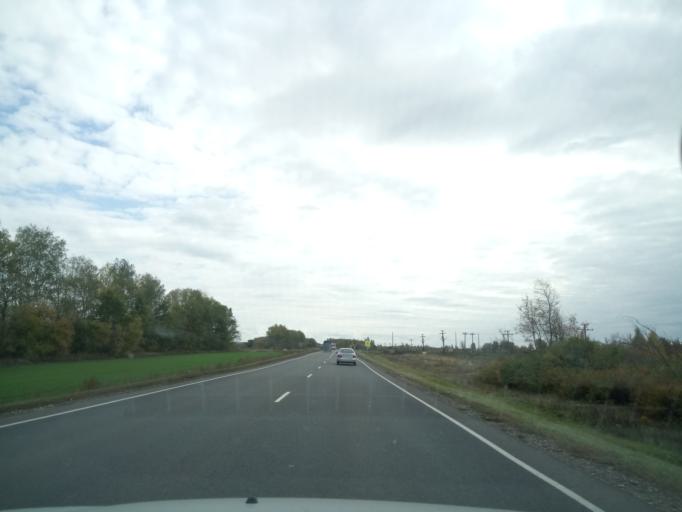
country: RU
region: Nizjnij Novgorod
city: Lukoyanov
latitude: 55.0700
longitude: 44.3421
